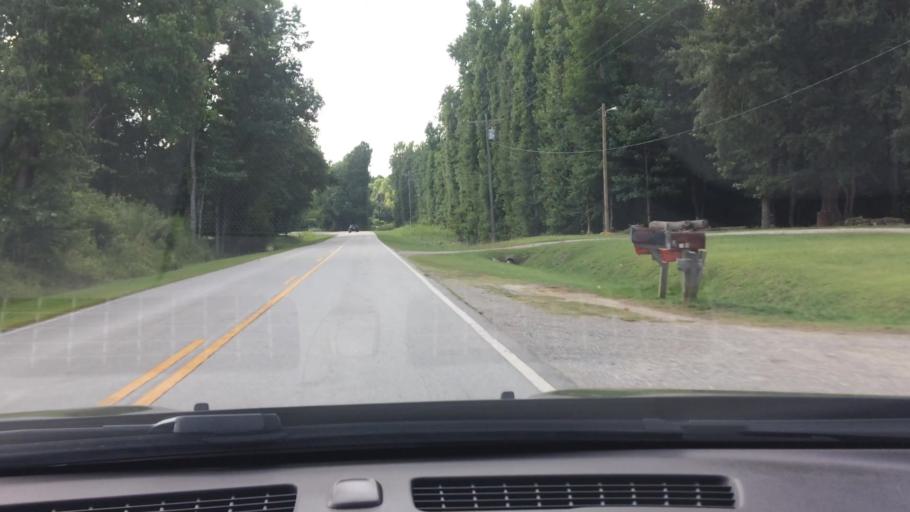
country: US
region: North Carolina
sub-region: Beaufort County
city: River Road
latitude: 35.4340
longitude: -76.9835
